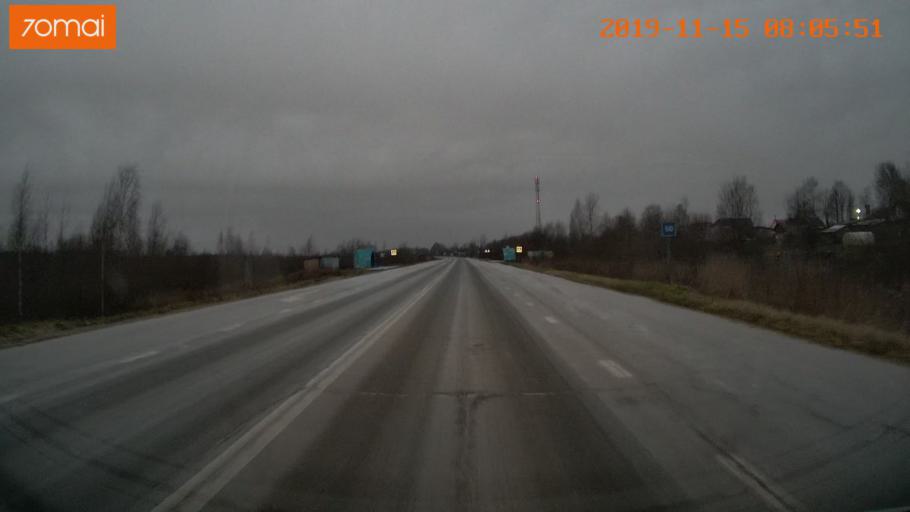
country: RU
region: Vologda
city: Cherepovets
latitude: 59.0188
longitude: 38.0502
